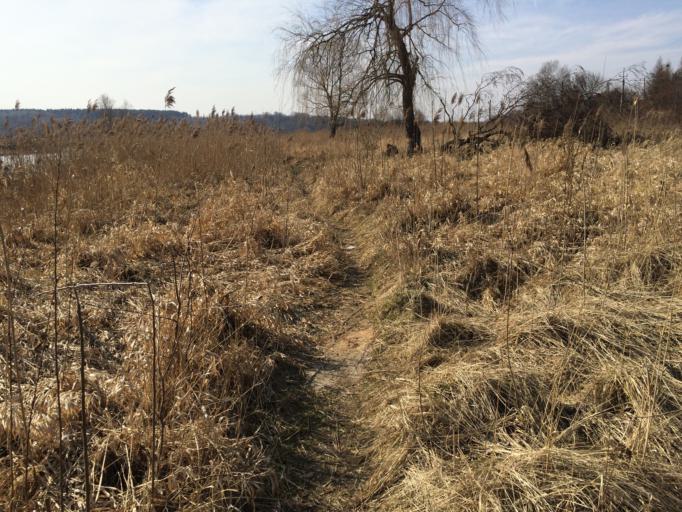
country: PL
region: Swietokrzyskie
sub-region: Powiat starachowicki
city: Starachowice
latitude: 51.0526
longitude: 21.0537
